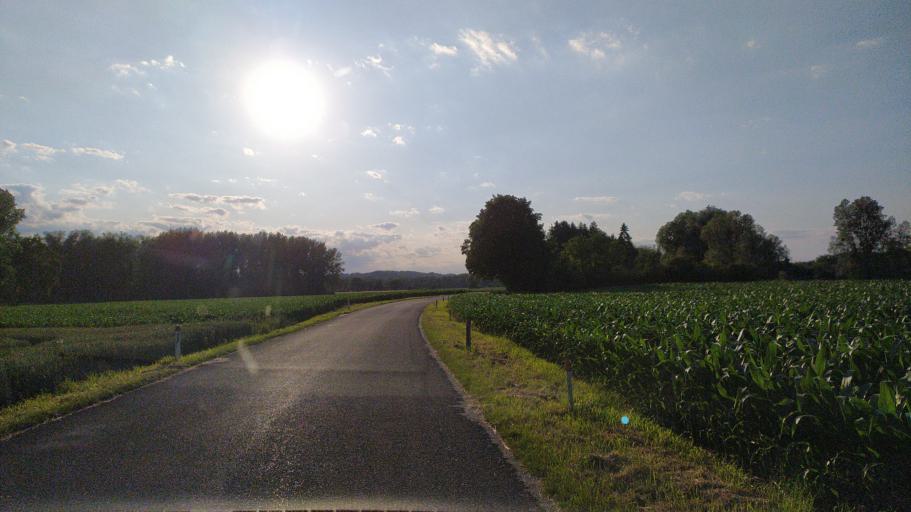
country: AT
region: Lower Austria
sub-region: Politischer Bezirk Amstetten
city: Strengberg
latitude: 48.1781
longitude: 14.6190
